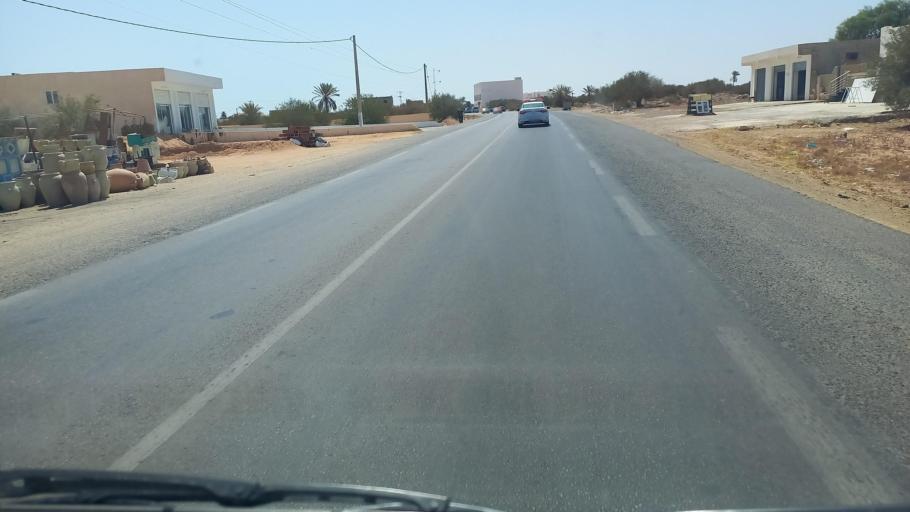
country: TN
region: Madanin
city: Houmt Souk
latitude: 33.8195
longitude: 10.8716
